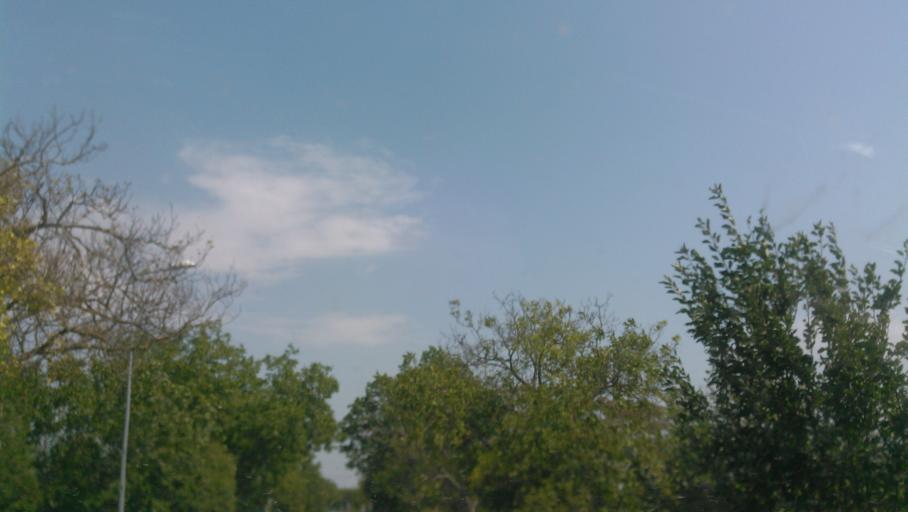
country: SK
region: Trnavsky
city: Samorin
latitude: 48.0507
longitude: 17.4618
